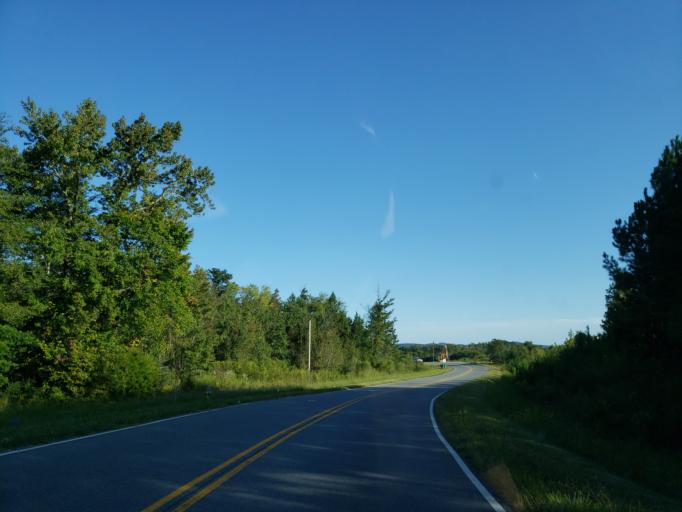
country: US
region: Georgia
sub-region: Bartow County
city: Rydal
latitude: 34.2773
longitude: -84.8071
